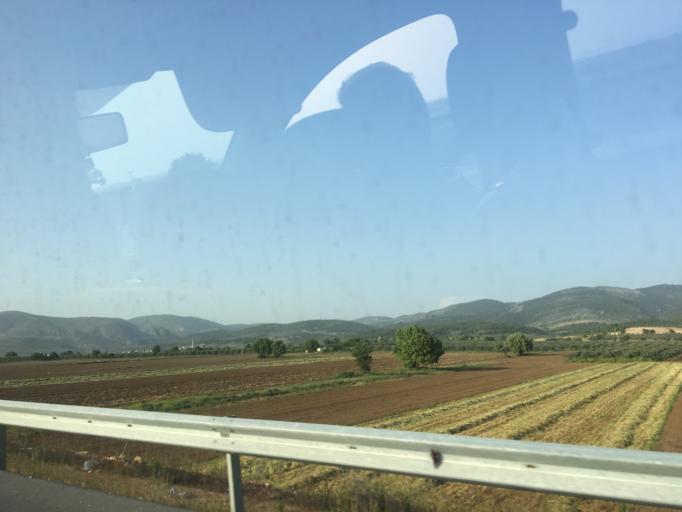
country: TR
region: Manisa
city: Golmarmara
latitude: 38.7950
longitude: 27.8978
